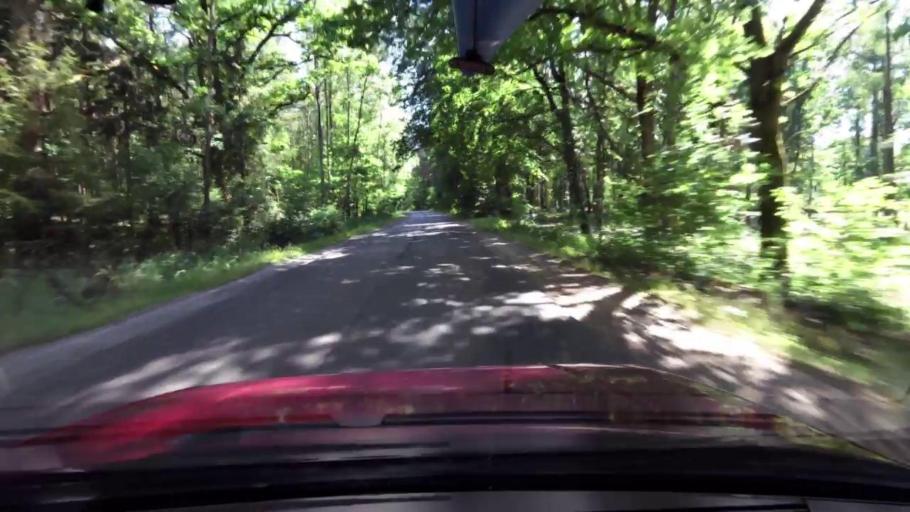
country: PL
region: Pomeranian Voivodeship
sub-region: Powiat slupski
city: Kobylnica
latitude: 54.3354
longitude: 16.9589
